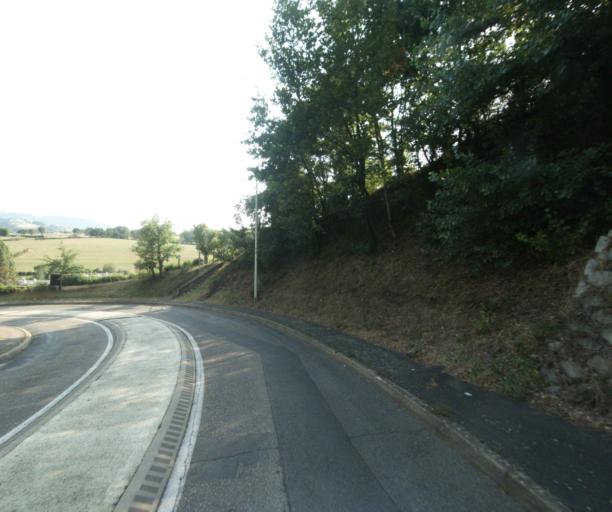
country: FR
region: Rhone-Alpes
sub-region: Departement du Rhone
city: Sain-Bel
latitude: 45.8129
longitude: 4.5957
